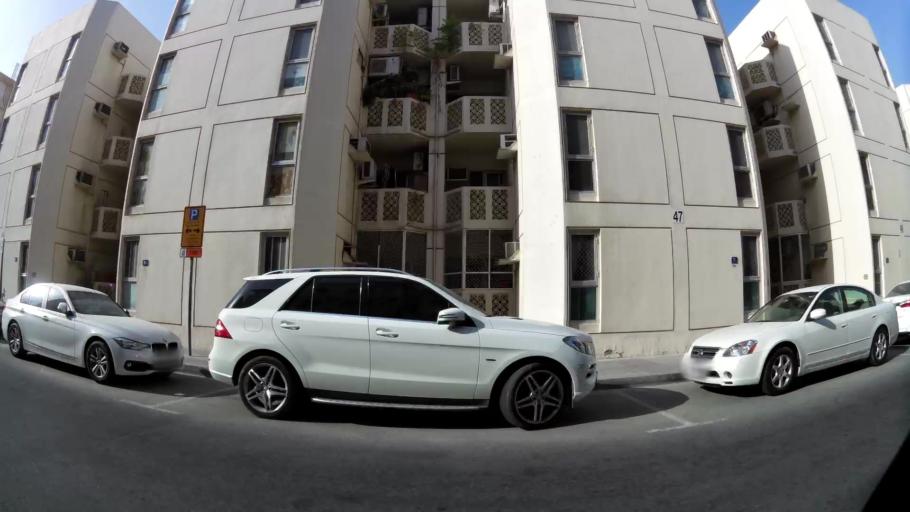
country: AE
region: Ash Shariqah
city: Sharjah
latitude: 25.2403
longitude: 55.2977
